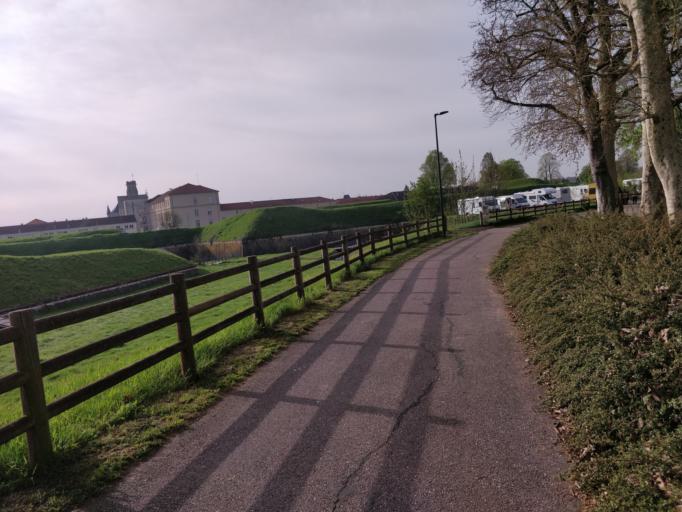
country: FR
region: Lorraine
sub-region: Departement de Meurthe-et-Moselle
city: Toul
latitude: 48.6774
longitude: 5.8851
